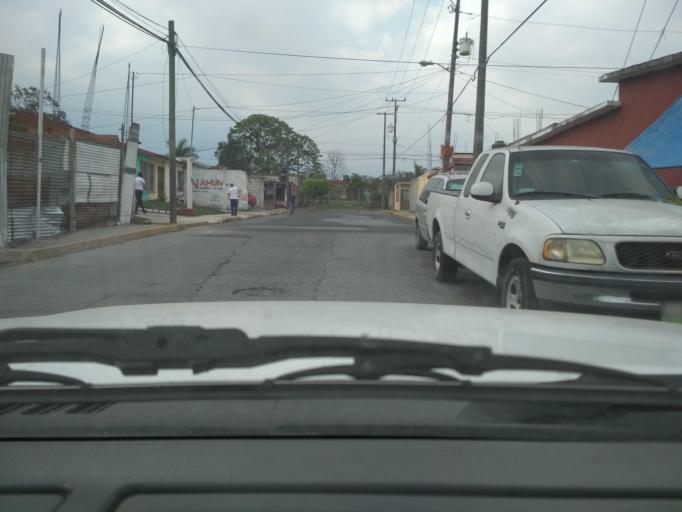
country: MX
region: Veracruz
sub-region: Mariano Escobedo
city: Palmira
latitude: 18.8741
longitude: -97.1013
